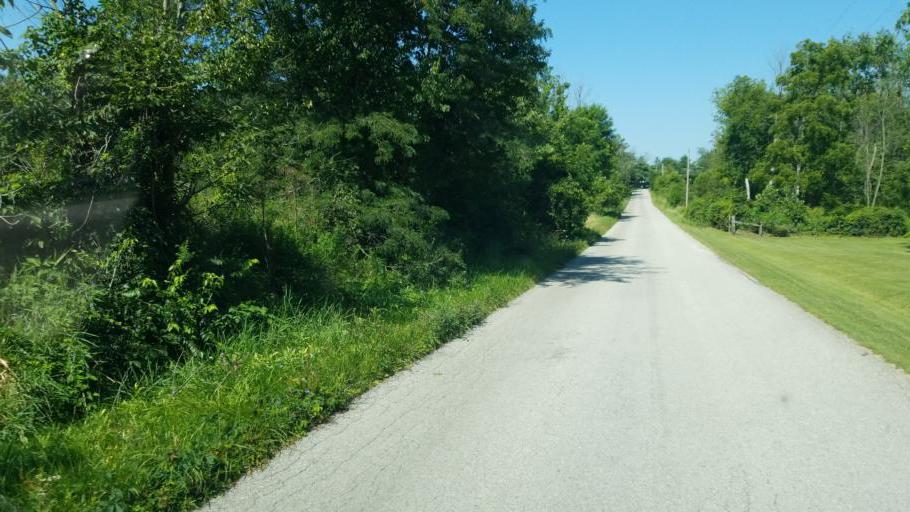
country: US
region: Ohio
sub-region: Morrow County
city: Cardington
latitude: 40.4333
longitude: -82.8304
